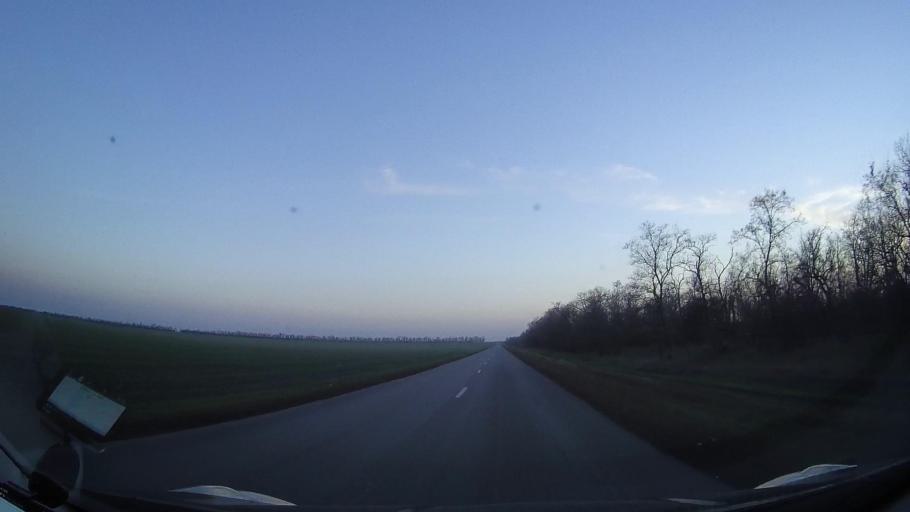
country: RU
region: Rostov
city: Zernograd
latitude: 46.9205
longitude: 40.3388
